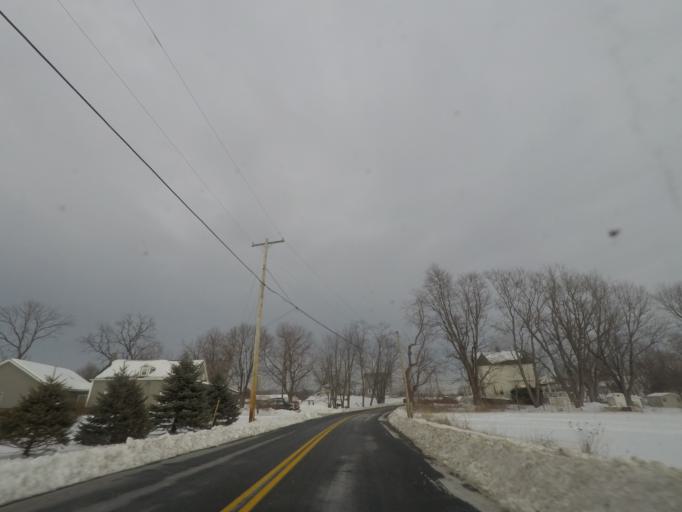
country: US
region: New York
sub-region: Rensselaer County
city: Castleton-on-Hudson
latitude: 42.5130
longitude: -73.7078
